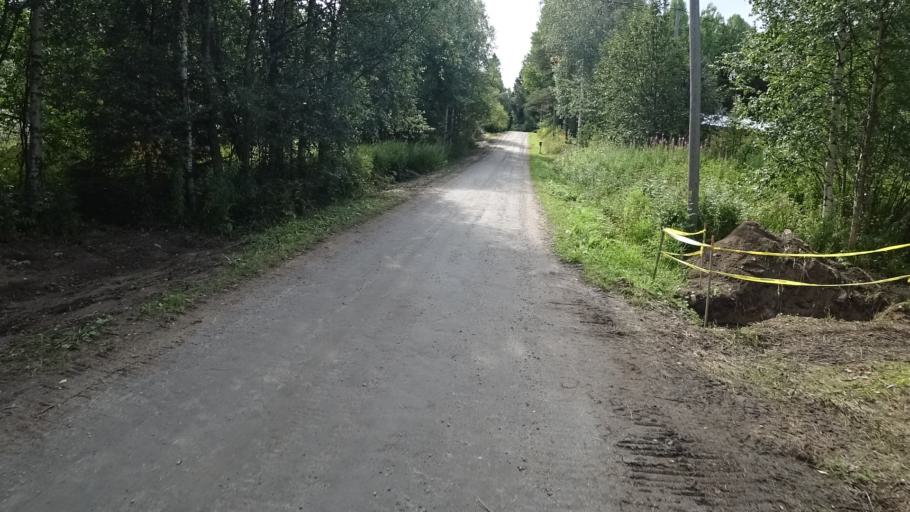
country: FI
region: North Karelia
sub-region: Joensuu
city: Ilomantsi
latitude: 62.6379
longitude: 31.2824
